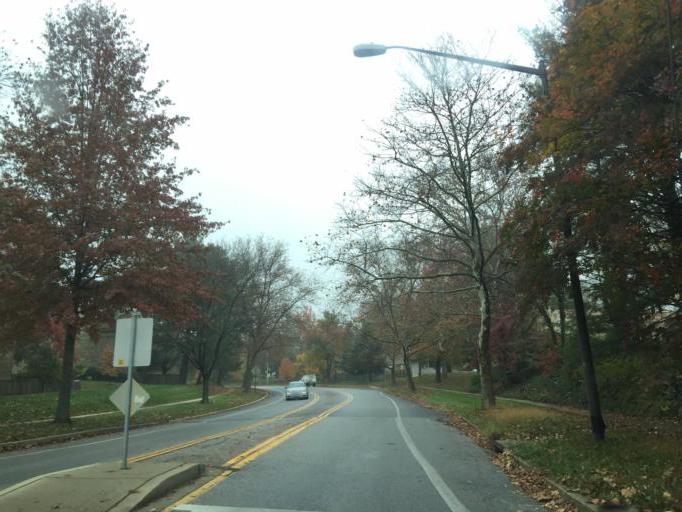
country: US
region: Maryland
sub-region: Howard County
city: Columbia
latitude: 39.1911
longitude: -76.8378
